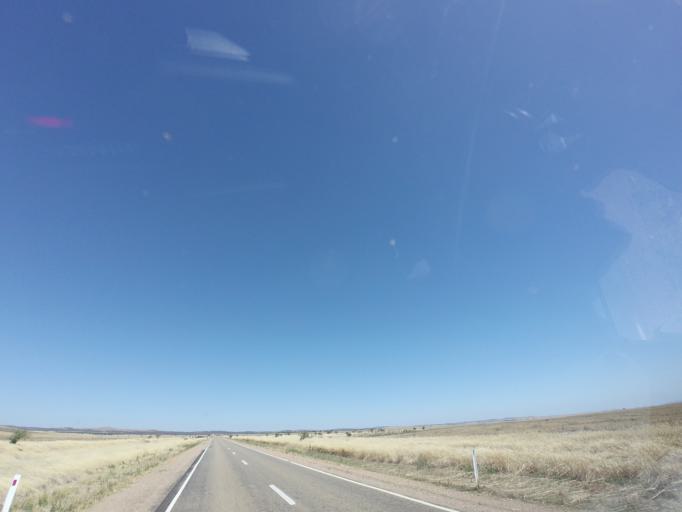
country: AU
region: South Australia
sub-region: Peterborough
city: Peterborough
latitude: -32.8340
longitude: 138.7132
